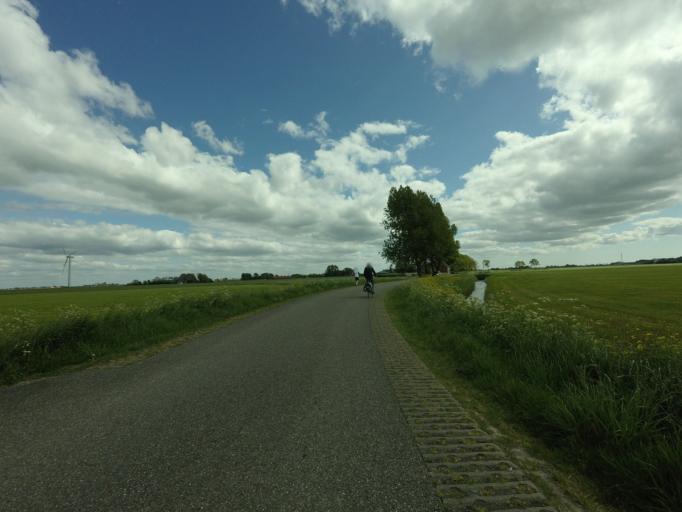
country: NL
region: Friesland
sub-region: Sudwest Fryslan
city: Bolsward
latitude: 53.0815
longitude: 5.5508
